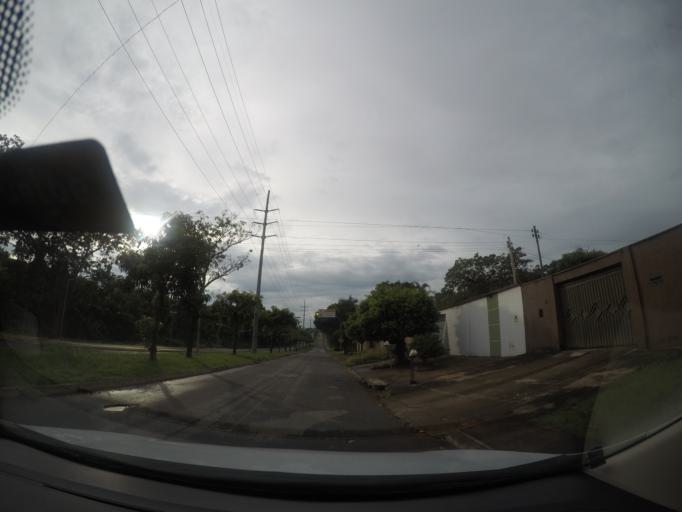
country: BR
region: Goias
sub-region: Goiania
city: Goiania
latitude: -16.7377
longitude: -49.3213
